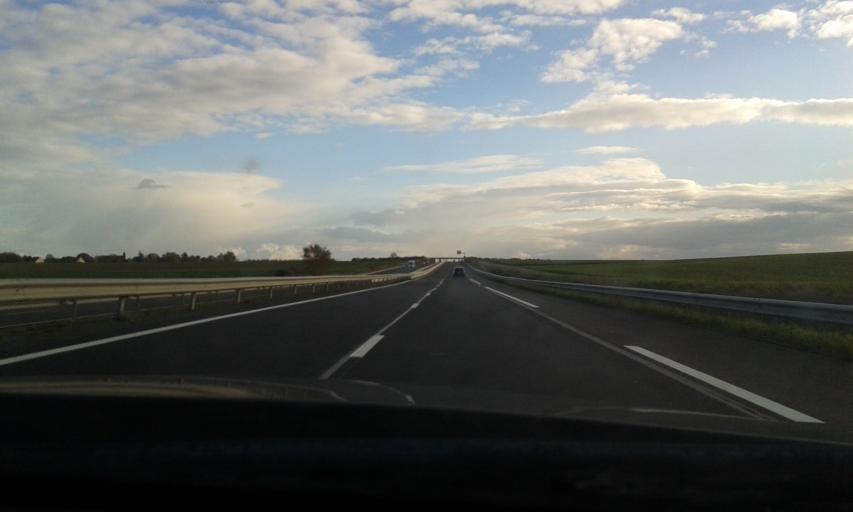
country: FR
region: Centre
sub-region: Departement d'Eure-et-Loir
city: Leves
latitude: 48.5155
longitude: 1.4599
